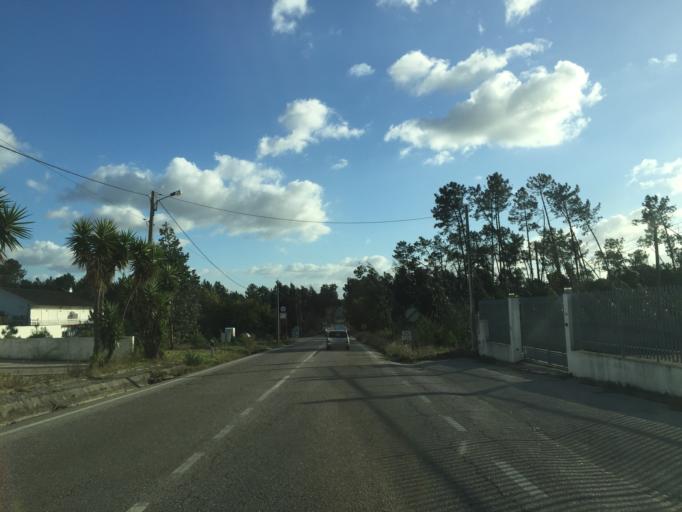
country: PT
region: Leiria
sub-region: Leiria
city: Monte Redondo
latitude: 39.8795
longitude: -8.8382
